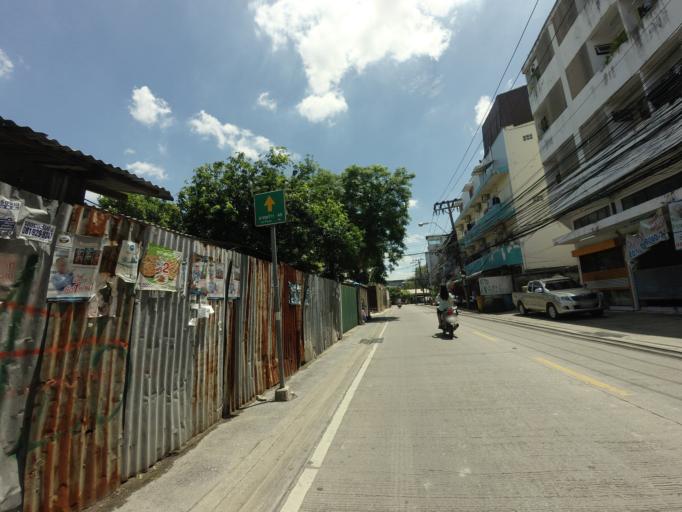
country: TH
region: Bangkok
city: Huai Khwang
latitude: 13.7961
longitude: 100.5852
